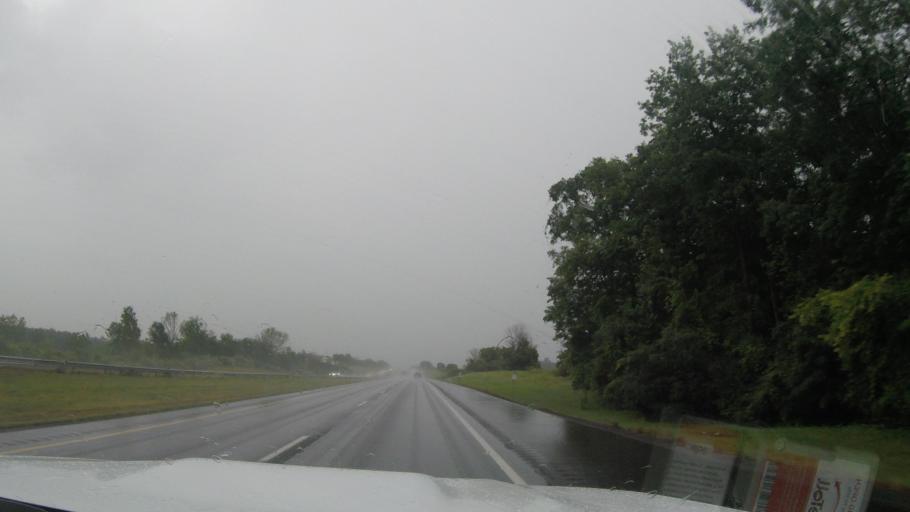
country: US
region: New York
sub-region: Ontario County
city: Phelps
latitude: 42.9555
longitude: -77.0174
